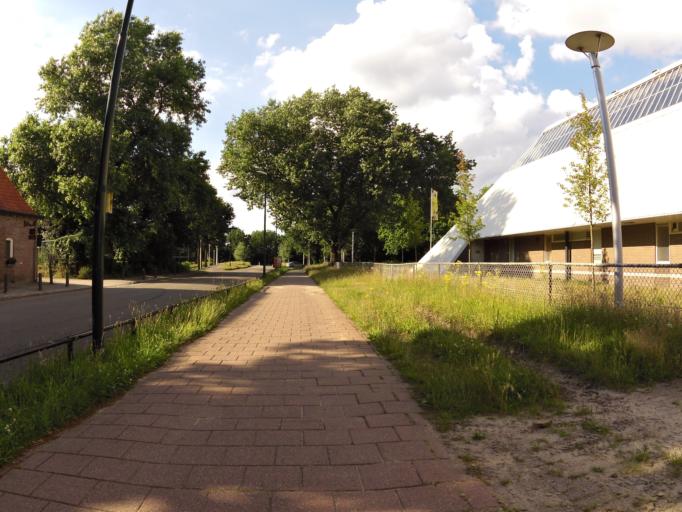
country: NL
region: North Brabant
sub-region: Gemeente Eindhoven
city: Eindhoven
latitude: 51.4152
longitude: 5.4709
